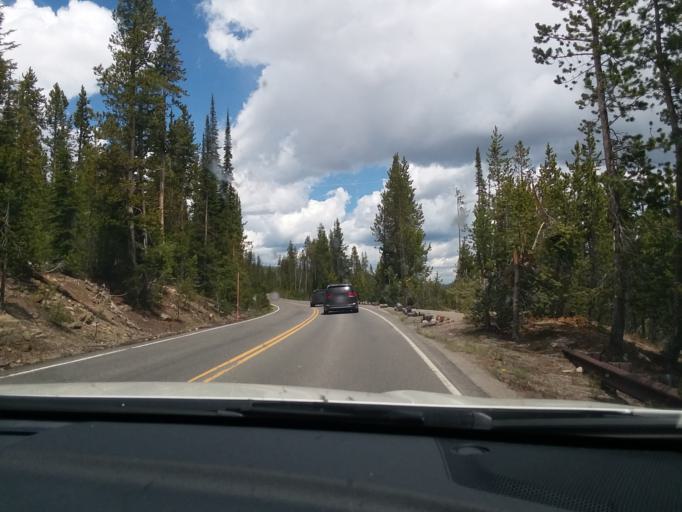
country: US
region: Montana
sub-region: Gallatin County
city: West Yellowstone
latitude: 44.2066
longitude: -110.6610
